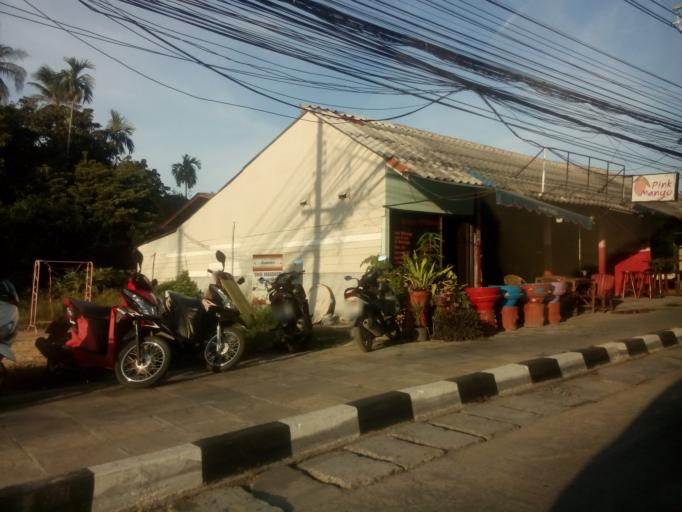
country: TH
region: Surat Thani
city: Ko Samui
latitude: 9.5739
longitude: 99.9870
